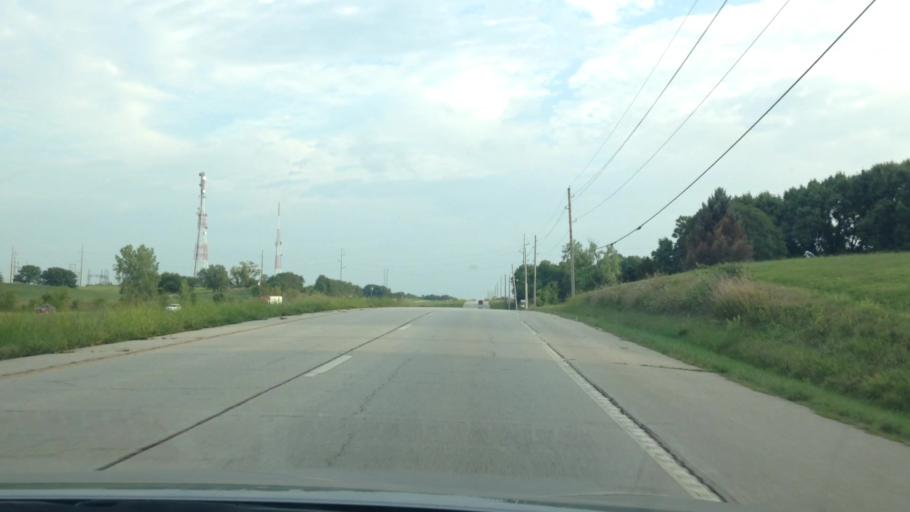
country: US
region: Missouri
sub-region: Clay County
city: Smithville
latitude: 39.3382
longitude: -94.5844
